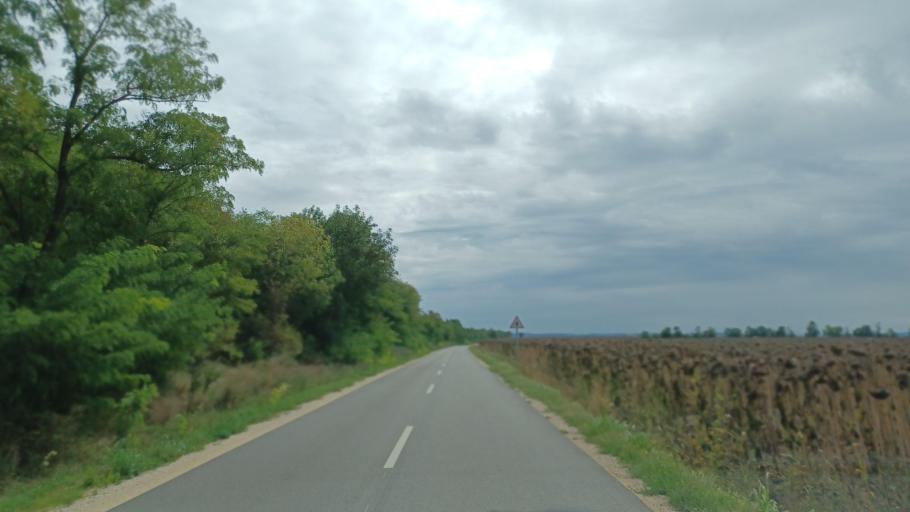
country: HU
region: Tolna
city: Zomba
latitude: 46.4191
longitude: 18.6107
